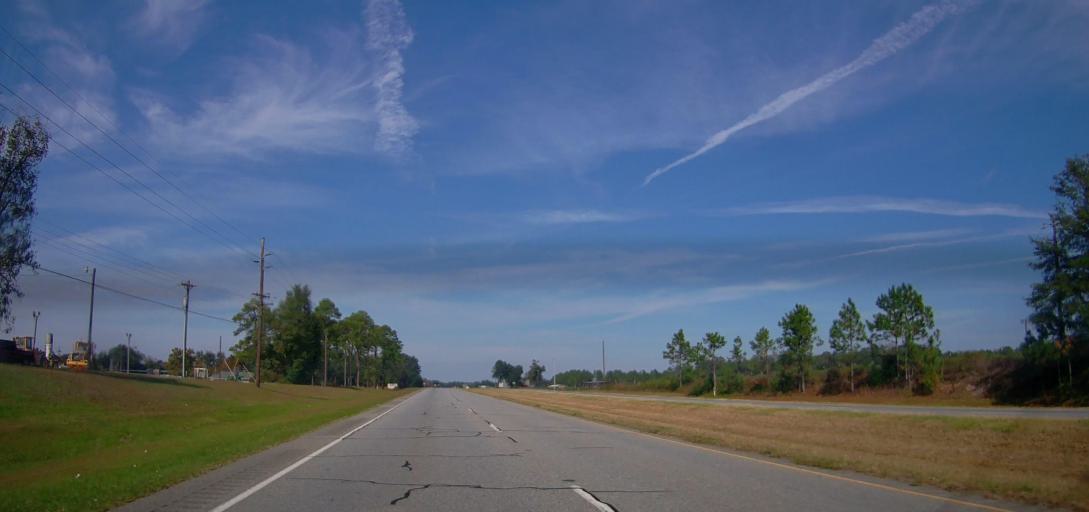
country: US
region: Georgia
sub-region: Mitchell County
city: Camilla
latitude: 31.3220
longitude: -84.1735
